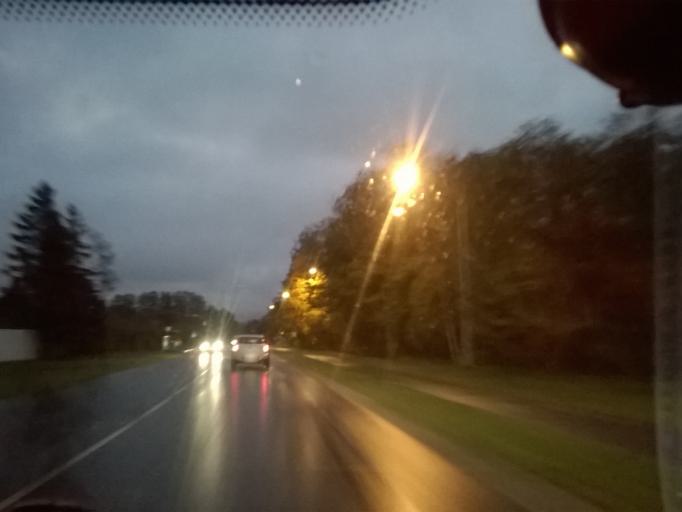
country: EE
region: Harju
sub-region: Viimsi vald
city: Haabneeme
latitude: 59.5167
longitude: 24.8131
